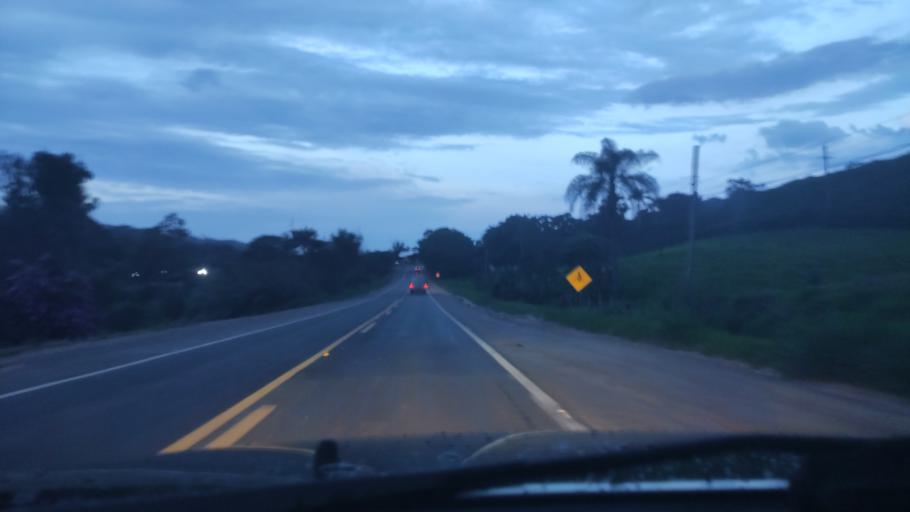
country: BR
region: Sao Paulo
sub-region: Socorro
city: Socorro
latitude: -22.6428
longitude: -46.5379
